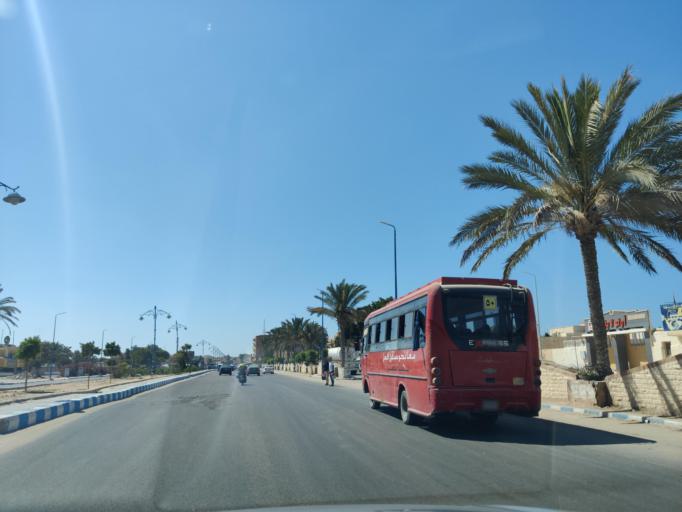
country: EG
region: Muhafazat Matruh
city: Mersa Matruh
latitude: 31.3394
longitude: 27.2500
